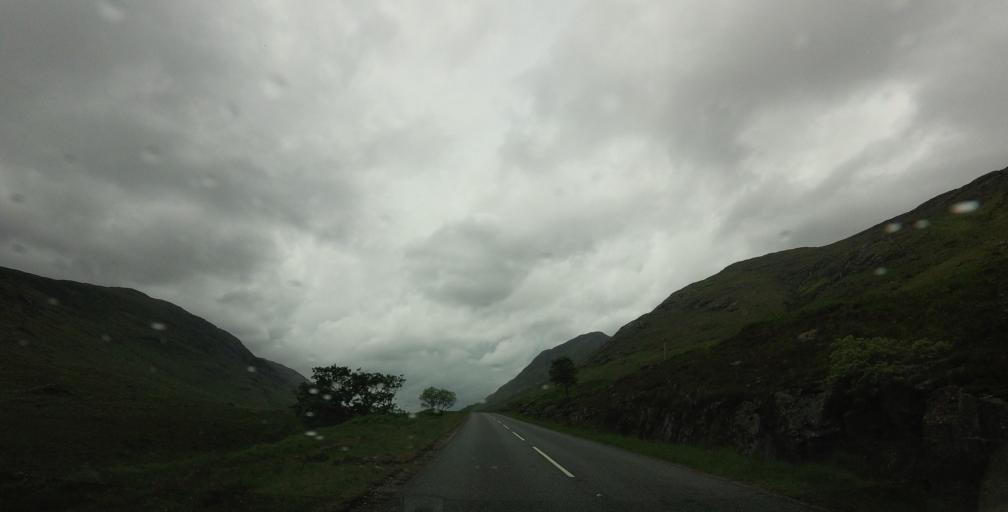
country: GB
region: Scotland
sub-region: Argyll and Bute
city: Oban
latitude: 56.6856
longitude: -5.4074
